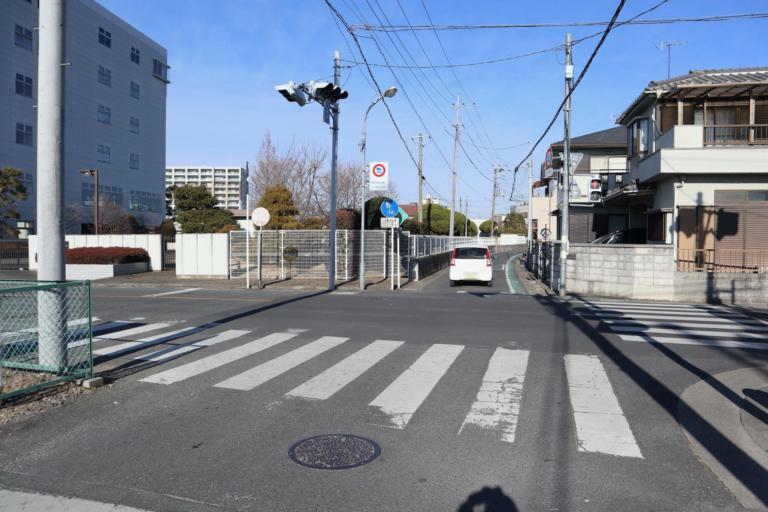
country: JP
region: Saitama
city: Fukiage-fujimi
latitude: 36.1025
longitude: 139.4503
